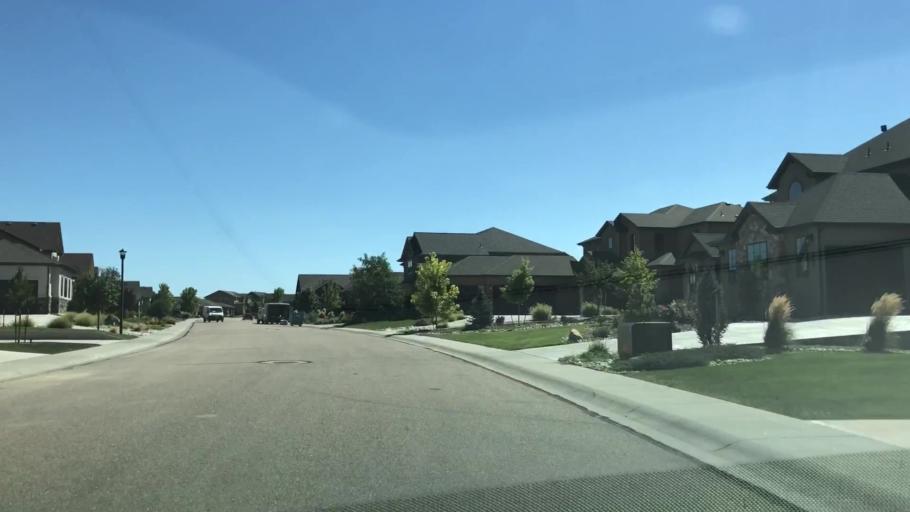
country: US
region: Colorado
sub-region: Weld County
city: Windsor
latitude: 40.4552
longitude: -104.9589
